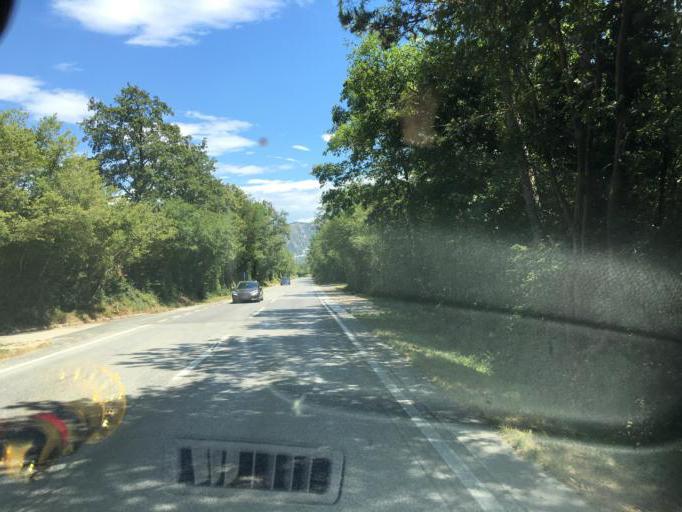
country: HR
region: Istarska
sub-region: Grad Labin
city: Labin
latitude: 45.1307
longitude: 14.1291
